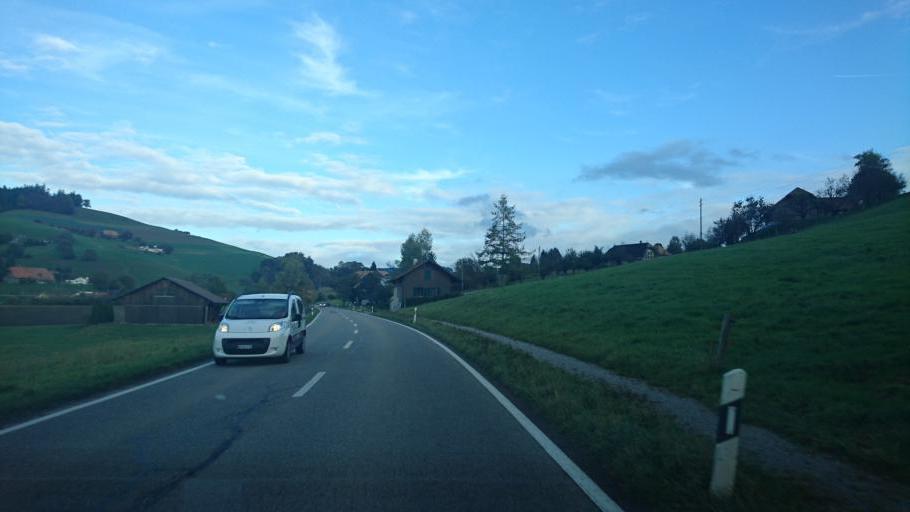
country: CH
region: Bern
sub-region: Bern-Mittelland District
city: Biglen
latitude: 46.9326
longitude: 7.6074
